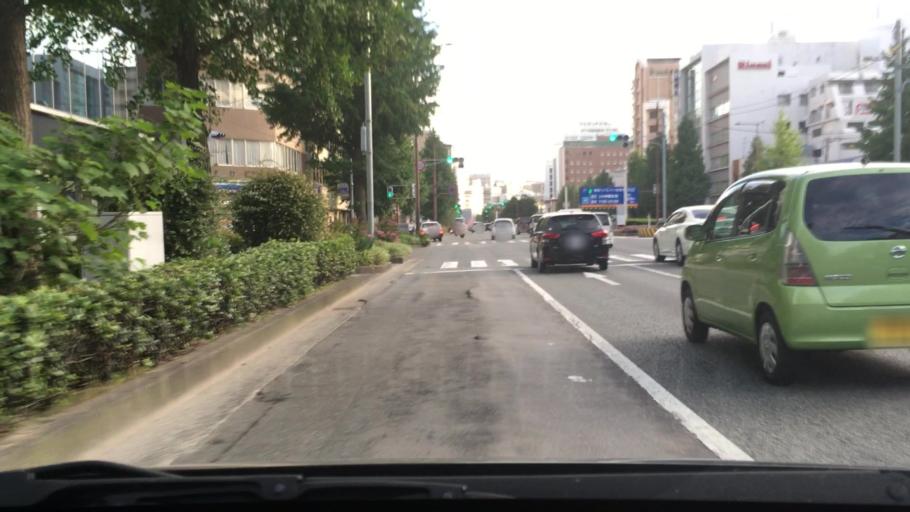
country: JP
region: Fukuoka
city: Fukuoka-shi
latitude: 33.5975
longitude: 130.4064
